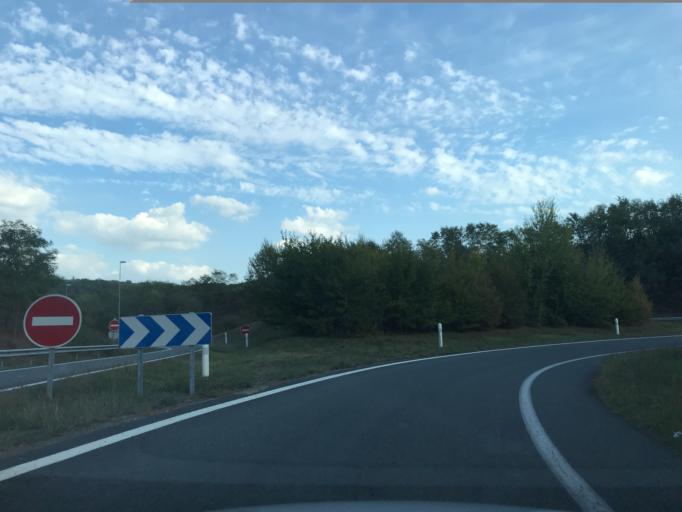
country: FR
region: Limousin
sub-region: Departement de la Correze
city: Saint-Pantaleon-de-Larche
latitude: 45.1630
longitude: 1.4383
